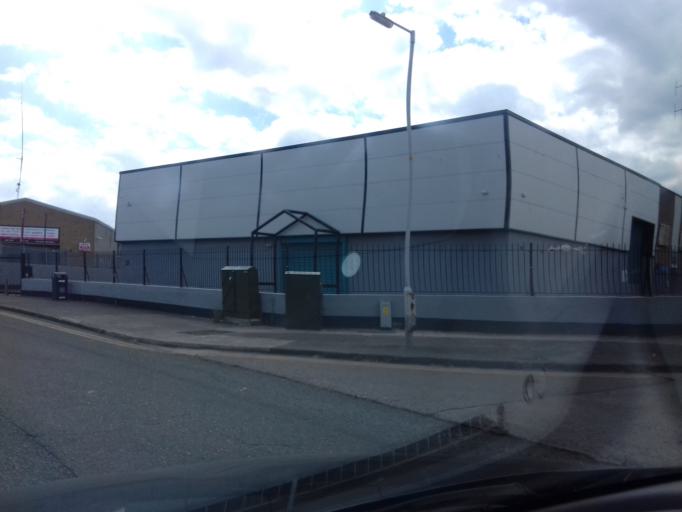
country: IE
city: Darndale
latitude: 53.3968
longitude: -6.1953
